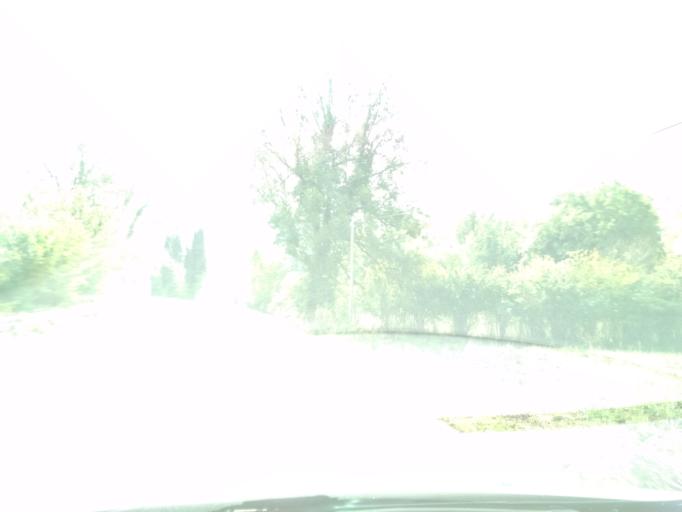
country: GR
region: Central Greece
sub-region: Nomos Evvoias
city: Prokopion
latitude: 38.7229
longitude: 23.5085
